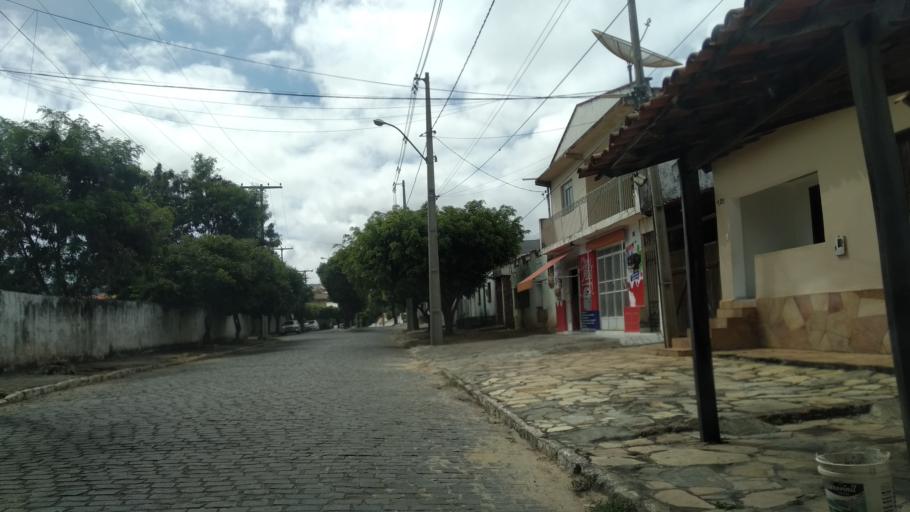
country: BR
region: Bahia
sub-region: Caetite
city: Caetite
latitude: -14.0693
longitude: -42.4947
